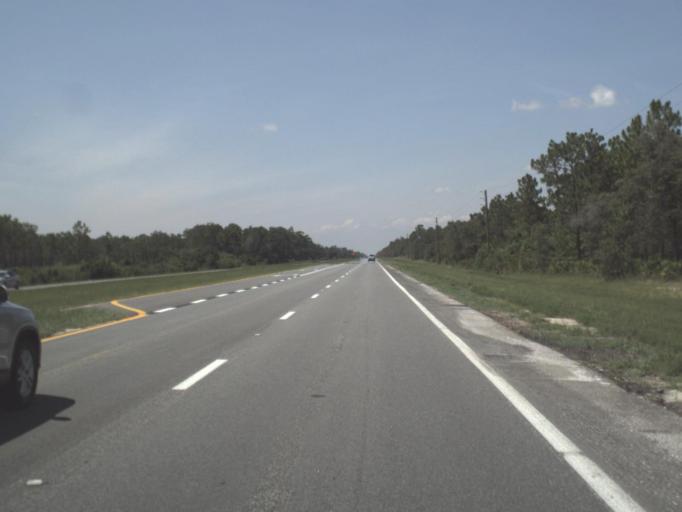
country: US
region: Florida
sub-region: Hernando County
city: North Weeki Wachee
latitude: 28.6219
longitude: -82.5518
